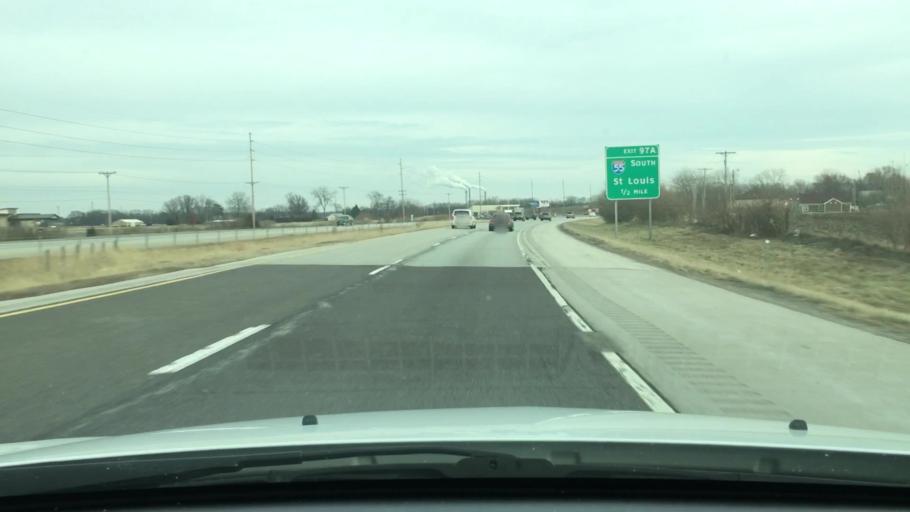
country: US
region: Illinois
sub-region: Sangamon County
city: Southern View
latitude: 39.7421
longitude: -89.6616
